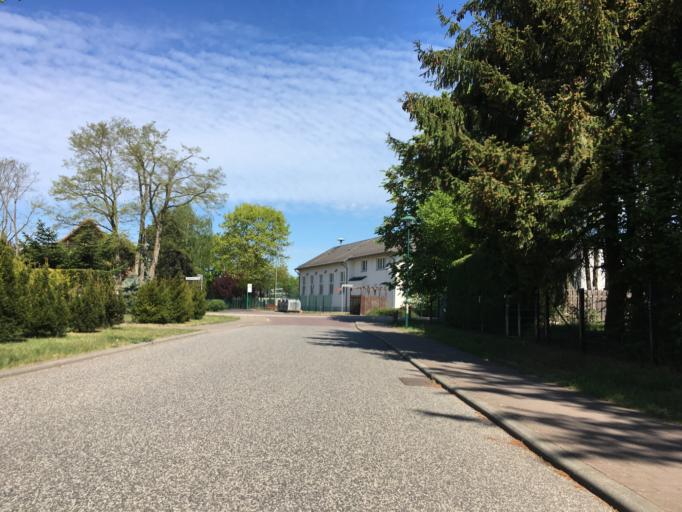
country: DE
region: Berlin
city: Buch
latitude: 52.6736
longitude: 13.5304
